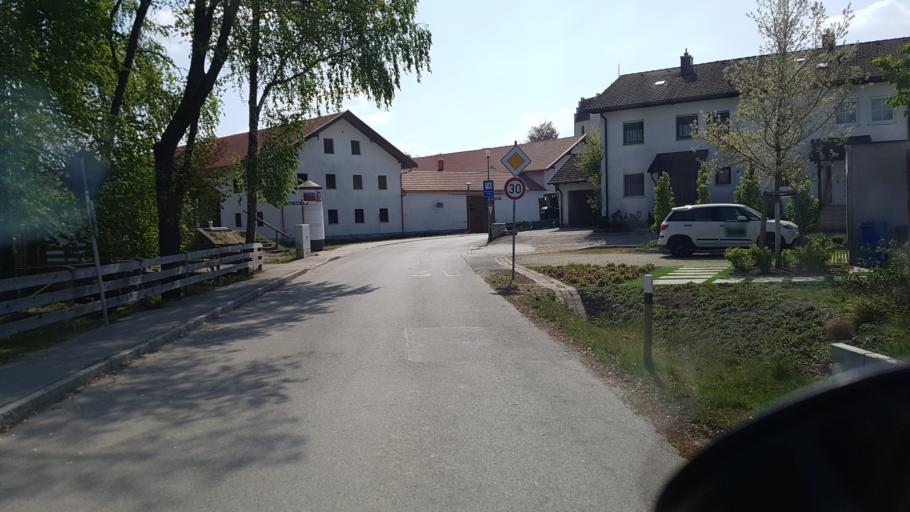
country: DE
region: Bavaria
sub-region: Upper Bavaria
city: Perach
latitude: 48.2424
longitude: 12.7517
